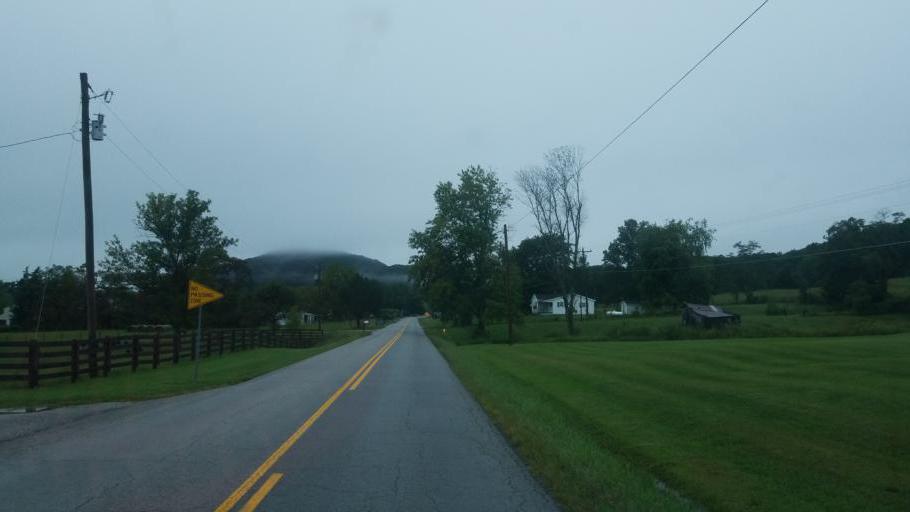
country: US
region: Kentucky
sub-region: Fleming County
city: Flemingsburg
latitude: 38.4043
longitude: -83.6354
